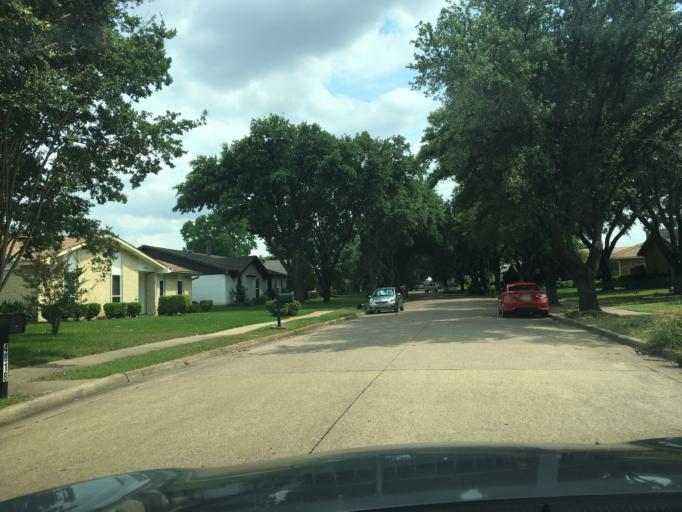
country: US
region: Texas
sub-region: Dallas County
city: Richardson
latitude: 32.9606
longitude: -96.6794
